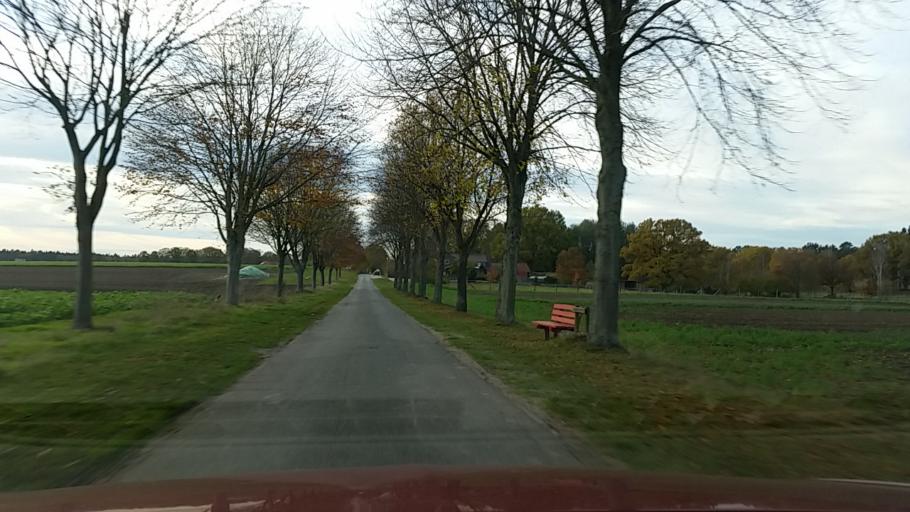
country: DE
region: Lower Saxony
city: Sprakensehl
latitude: 52.8074
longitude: 10.5358
